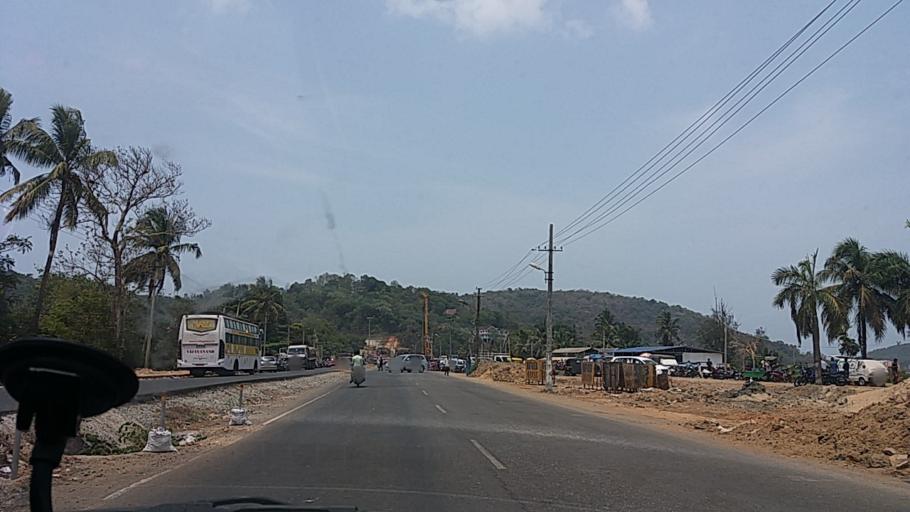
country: IN
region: Karnataka
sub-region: Uttar Kannada
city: Karwar
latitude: 14.8091
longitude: 74.1268
